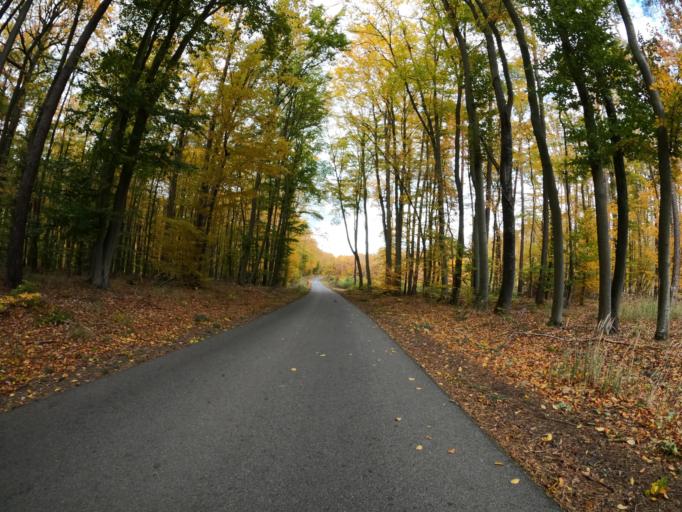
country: PL
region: West Pomeranian Voivodeship
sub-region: Powiat mysliborski
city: Barlinek
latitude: 52.9423
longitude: 15.2840
